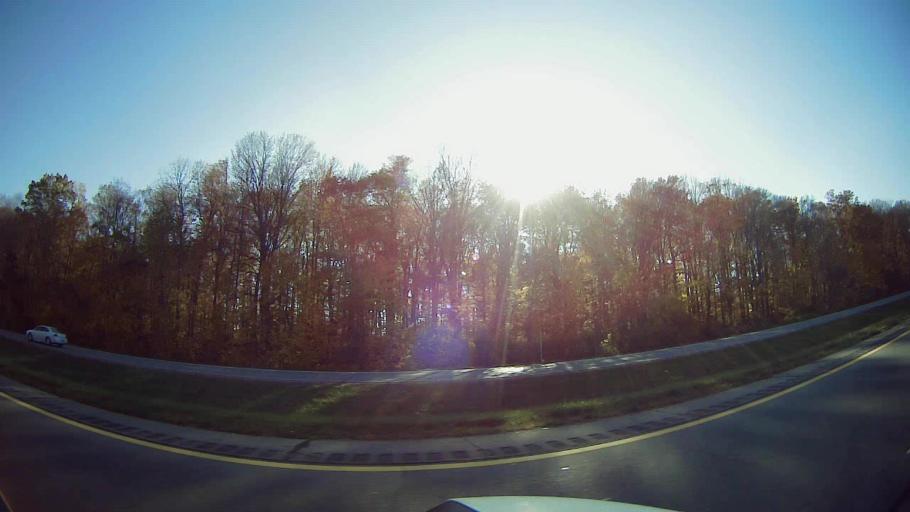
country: US
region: Michigan
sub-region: Oakland County
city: Farmington
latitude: 42.4611
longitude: -83.4079
